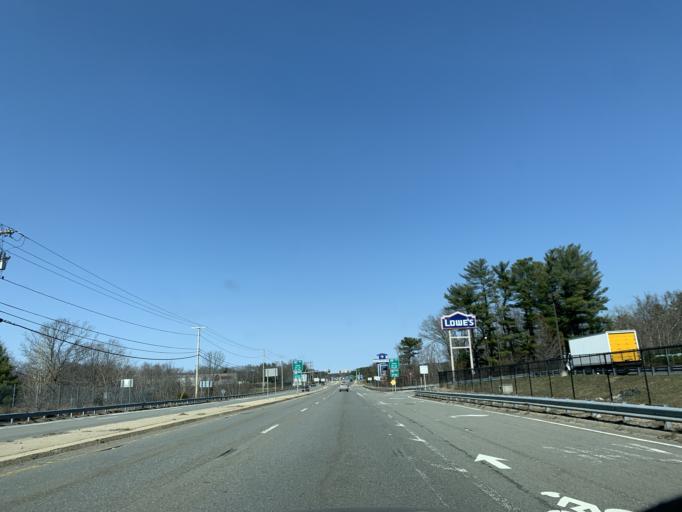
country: US
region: Massachusetts
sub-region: Norfolk County
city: Plainville
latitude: 42.0302
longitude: -71.3099
